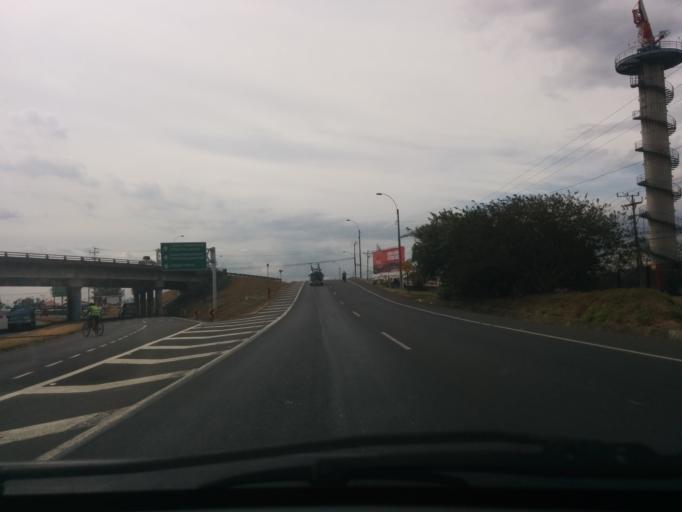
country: CR
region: Alajuela
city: Alajuela
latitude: 9.9999
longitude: -84.2012
